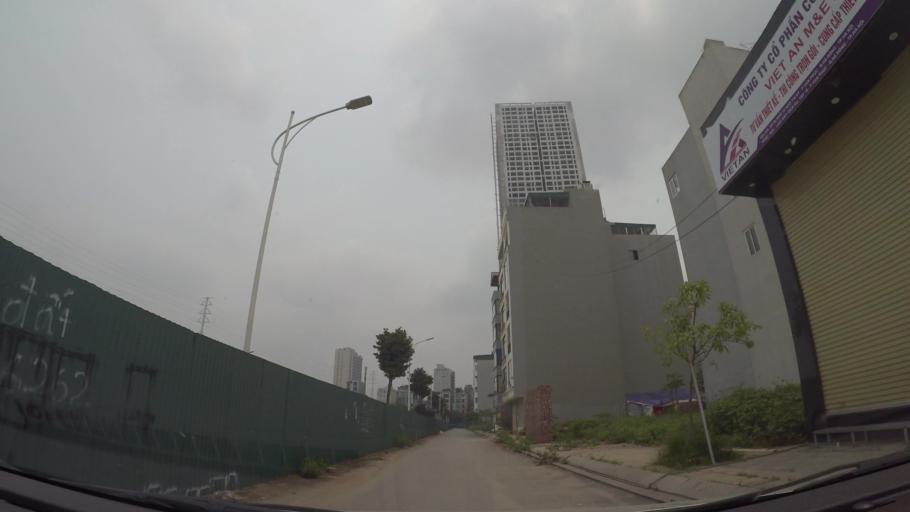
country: VN
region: Ha Noi
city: Ha Dong
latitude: 20.9804
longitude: 105.7691
